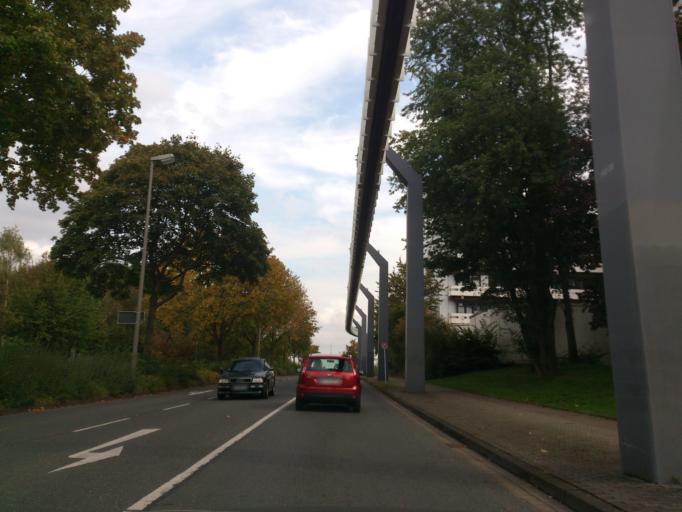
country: DE
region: North Rhine-Westphalia
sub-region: Regierungsbezirk Arnsberg
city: Dortmund
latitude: 51.4945
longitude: 7.4160
